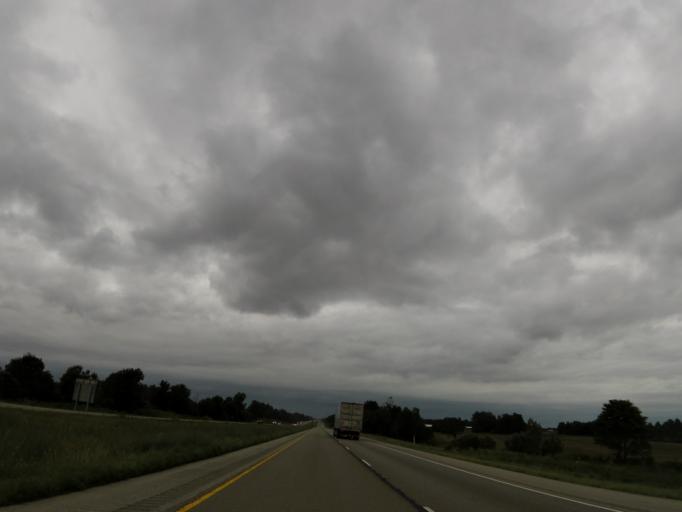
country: US
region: Illinois
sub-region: Massac County
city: Metropolis
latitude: 37.1936
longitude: -88.6869
